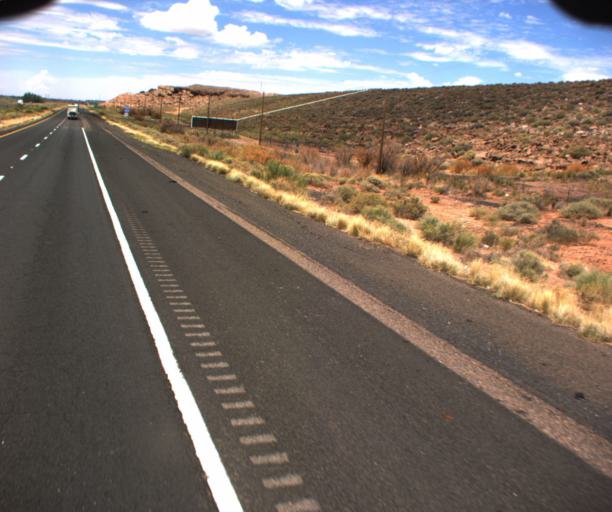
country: US
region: Arizona
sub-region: Navajo County
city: Joseph City
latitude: 34.9274
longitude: -110.2667
